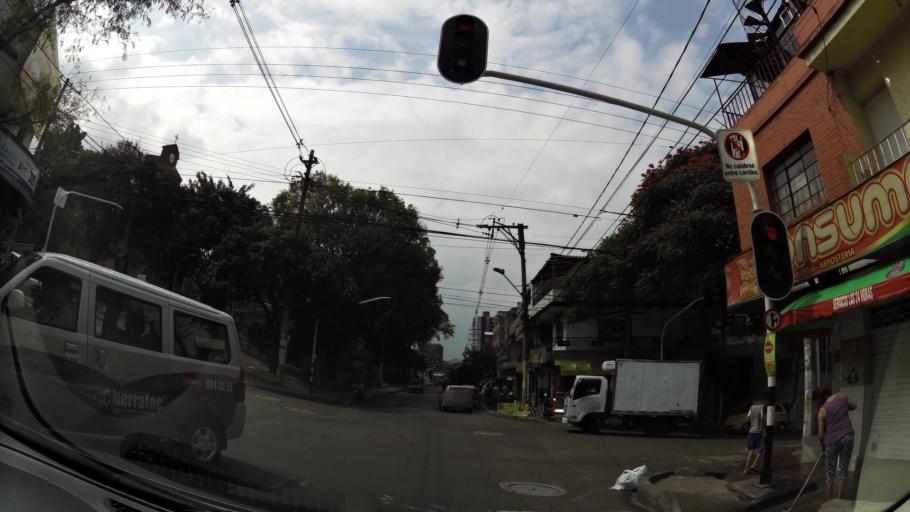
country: CO
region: Antioquia
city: Medellin
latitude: 6.2719
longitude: -75.5583
